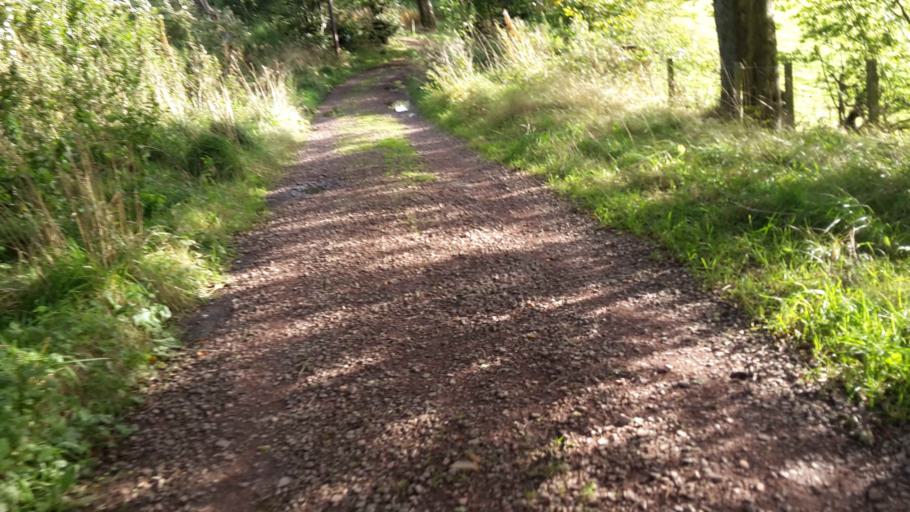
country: GB
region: Scotland
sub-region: South Lanarkshire
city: Carluke
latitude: 55.7234
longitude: -3.8281
